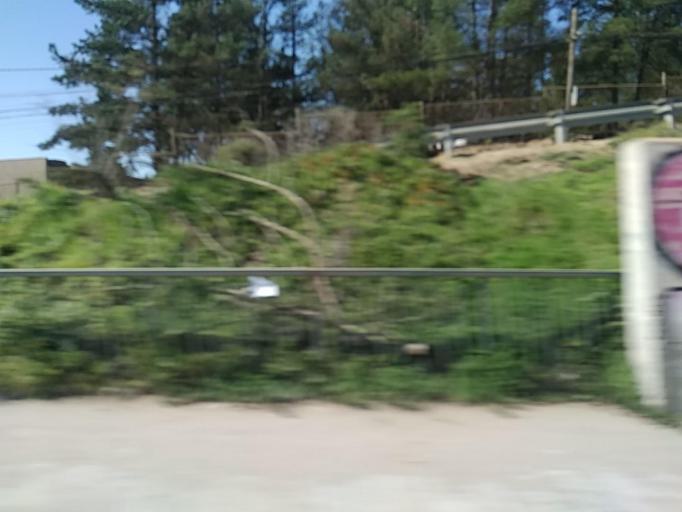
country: CL
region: Valparaiso
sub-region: Provincia de Valparaiso
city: Vina del Mar
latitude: -32.9539
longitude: -71.5389
